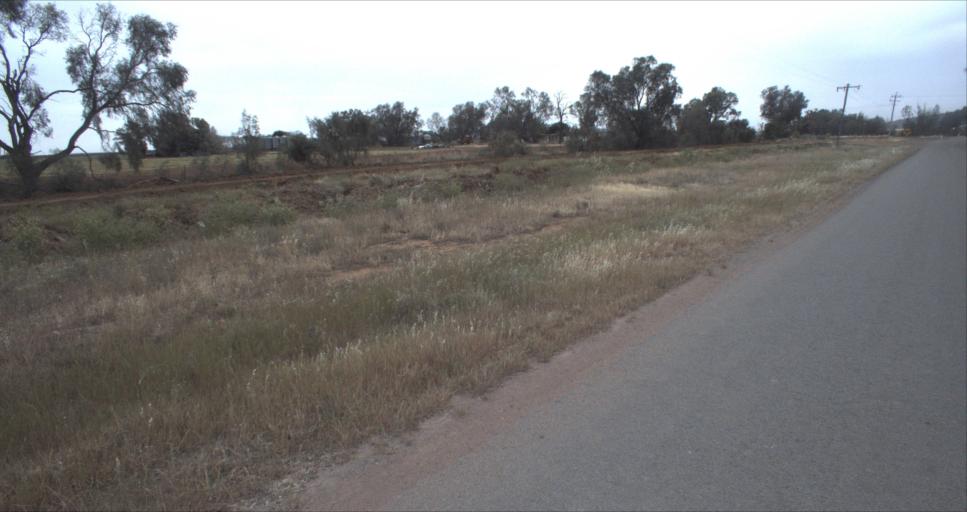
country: AU
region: New South Wales
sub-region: Leeton
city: Leeton
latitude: -34.4442
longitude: 146.3750
